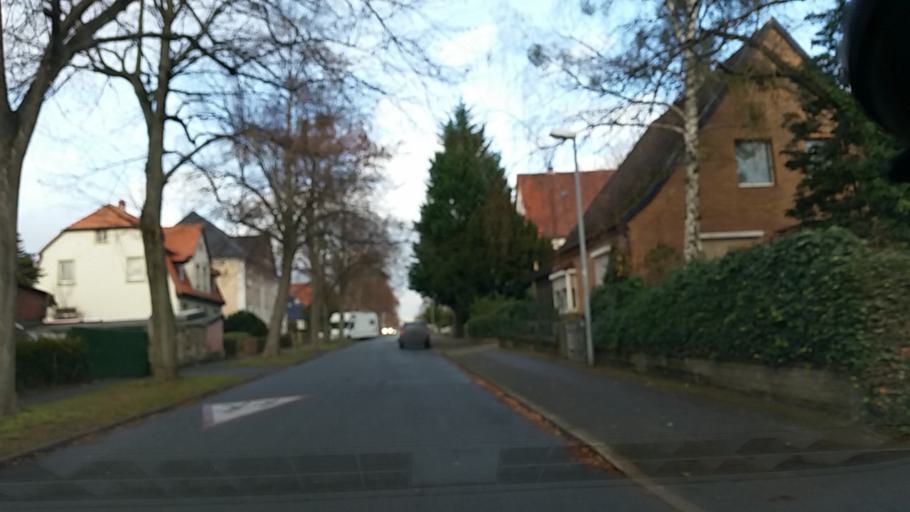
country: DE
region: Lower Saxony
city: Wolfsburg
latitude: 52.4388
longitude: 10.8343
